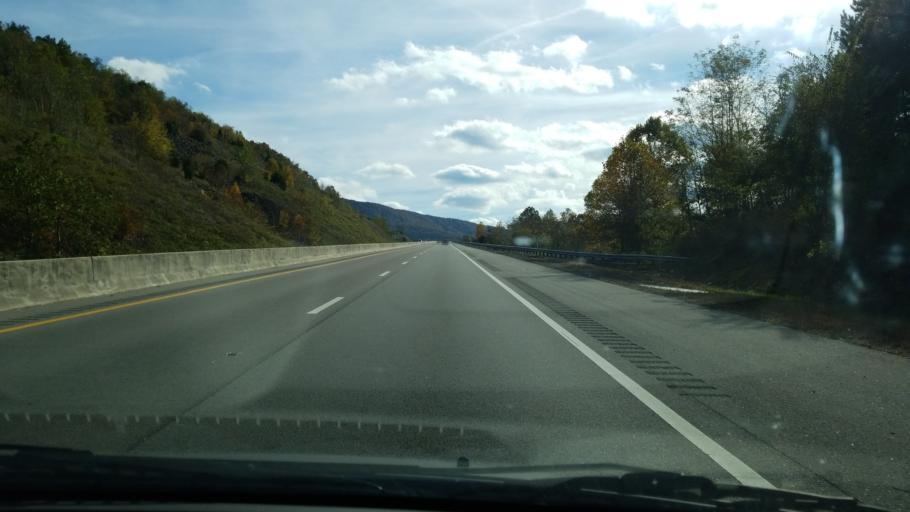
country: US
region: Tennessee
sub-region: Sequatchie County
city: Dunlap
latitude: 35.3788
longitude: -85.3311
